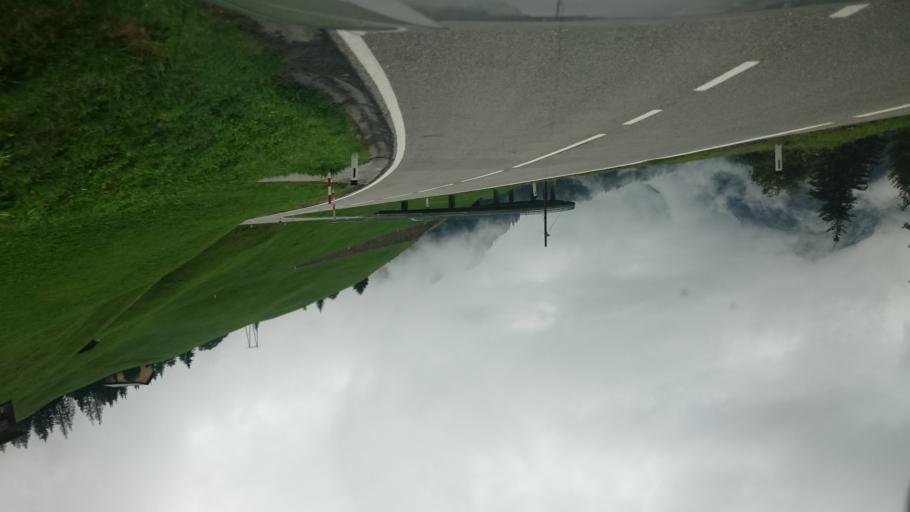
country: AT
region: Vorarlberg
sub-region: Politischer Bezirk Bregenz
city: Schroecken
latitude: 47.2597
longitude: 10.0947
